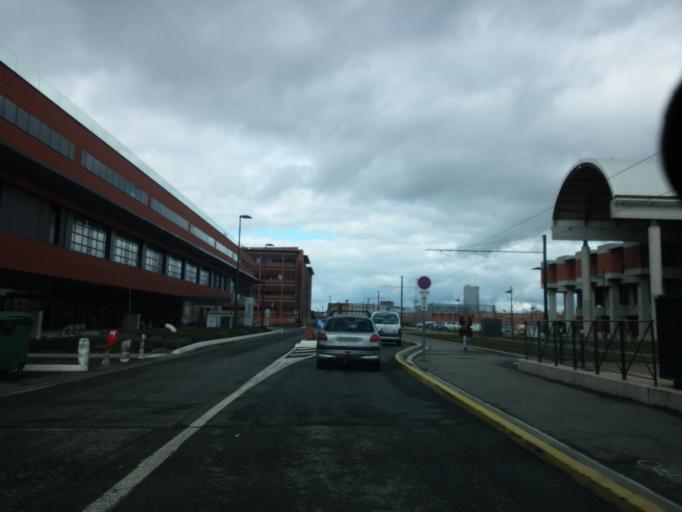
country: FR
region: Midi-Pyrenees
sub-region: Departement de la Haute-Garonne
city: Blagnac
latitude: 43.6091
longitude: 1.4018
